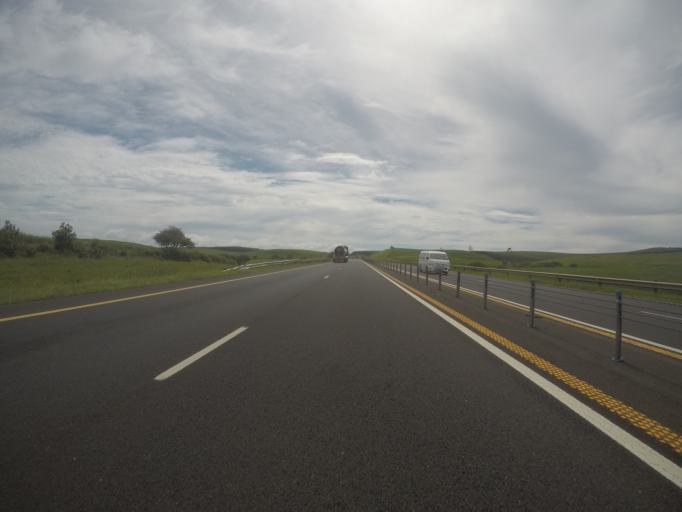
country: ZA
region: KwaZulu-Natal
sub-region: uThungulu District Municipality
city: Eshowe
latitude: -29.0520
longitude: 31.6356
